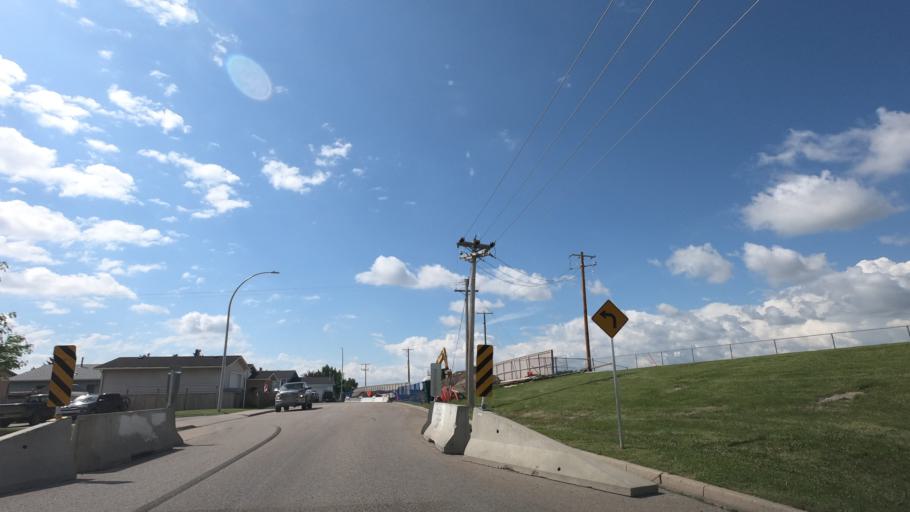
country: CA
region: Alberta
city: Airdrie
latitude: 51.2858
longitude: -114.0178
